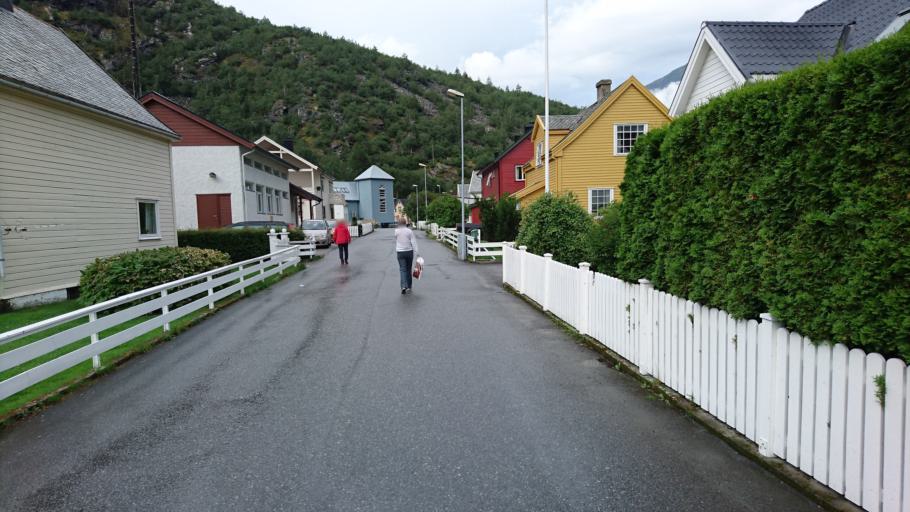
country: NO
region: Sogn og Fjordane
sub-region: Ardal
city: Farnes
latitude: 61.3098
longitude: 7.8022
